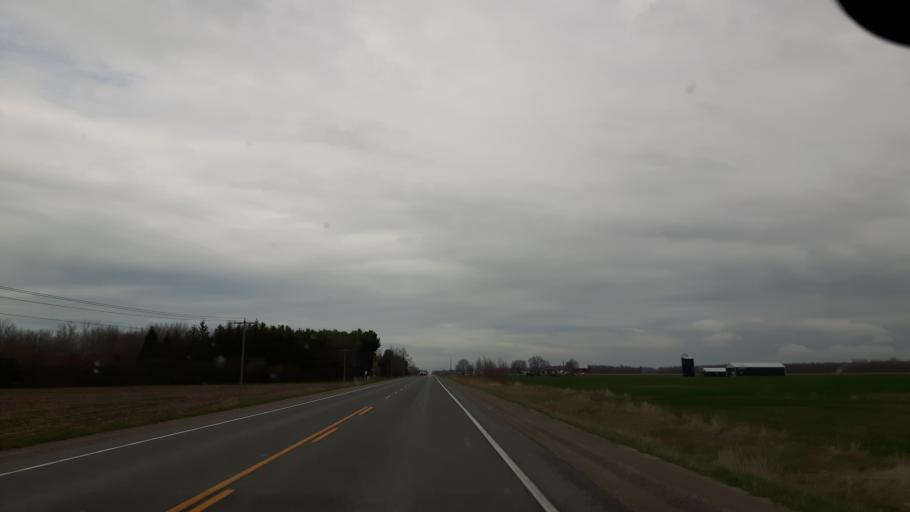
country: CA
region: Ontario
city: Goderich
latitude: 43.6184
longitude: -81.7056
